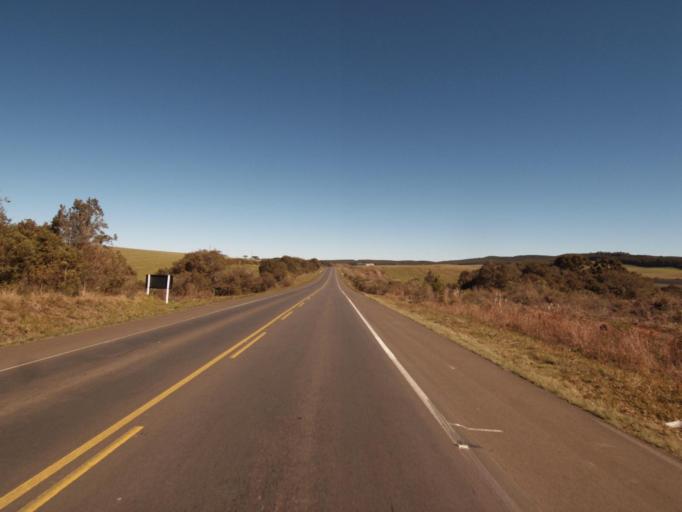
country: BR
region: Santa Catarina
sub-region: Concordia
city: Concordia
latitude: -26.9087
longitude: -51.9131
